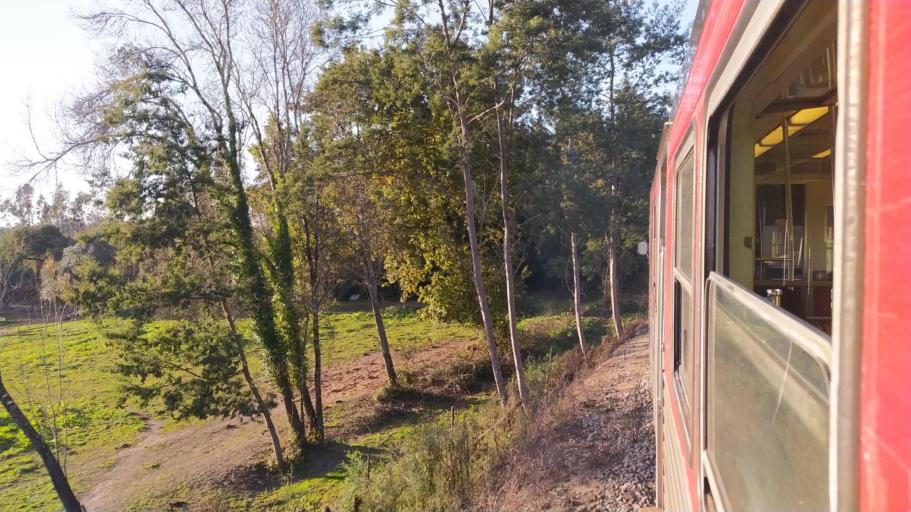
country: PT
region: Aveiro
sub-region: Aveiro
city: Eixo
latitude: 40.6015
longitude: -8.5258
